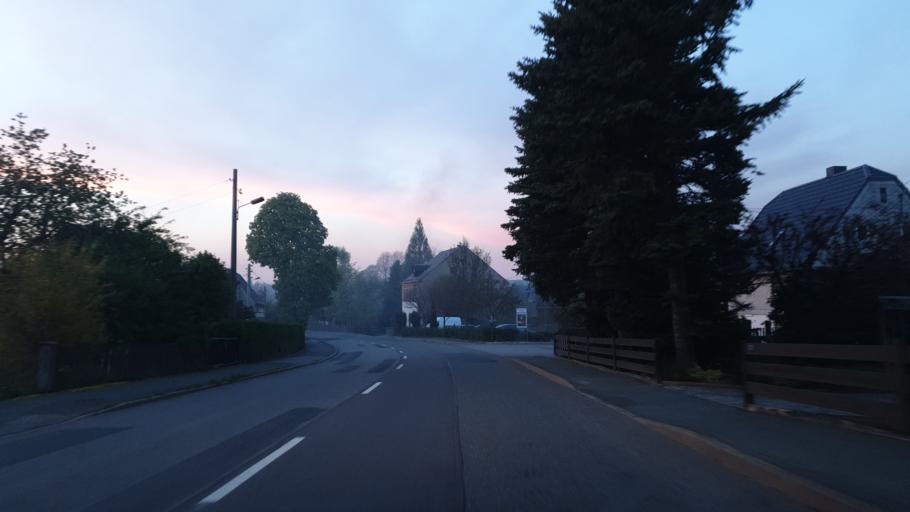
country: DE
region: Saxony
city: Stollberg
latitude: 50.6737
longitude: 12.7656
